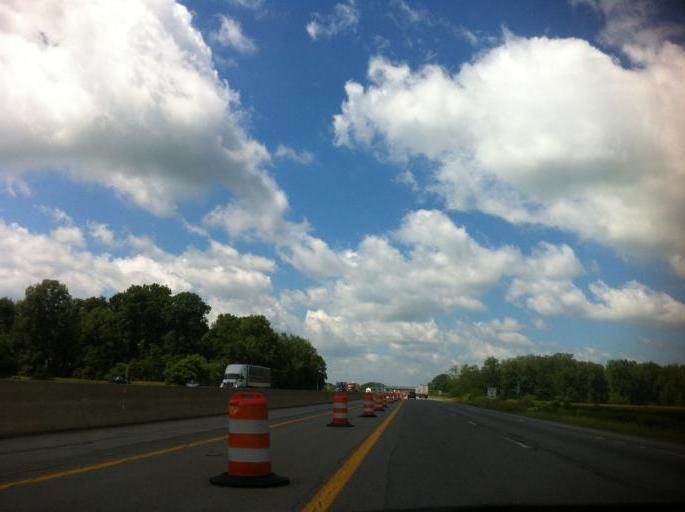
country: US
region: Ohio
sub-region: Huron County
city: Bellevue
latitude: 41.3476
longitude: -82.8072
